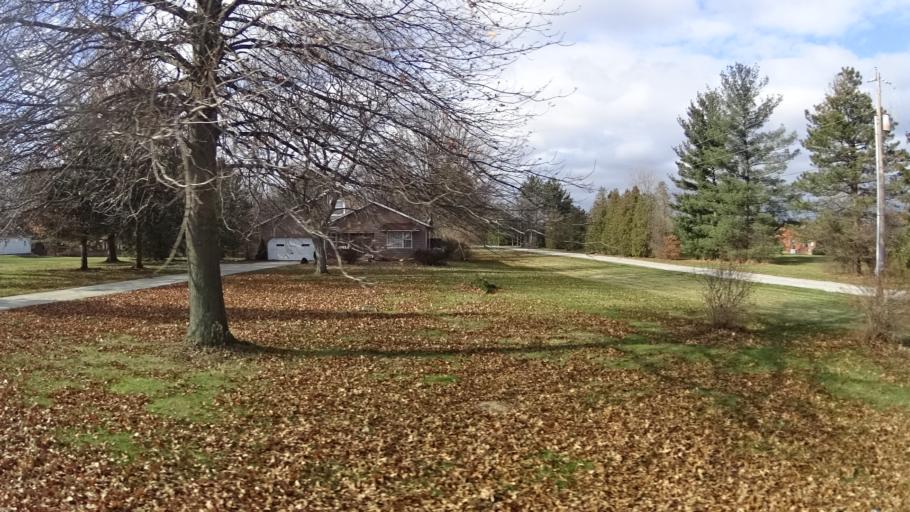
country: US
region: Ohio
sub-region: Lorain County
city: Camden
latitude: 41.2621
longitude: -82.2893
